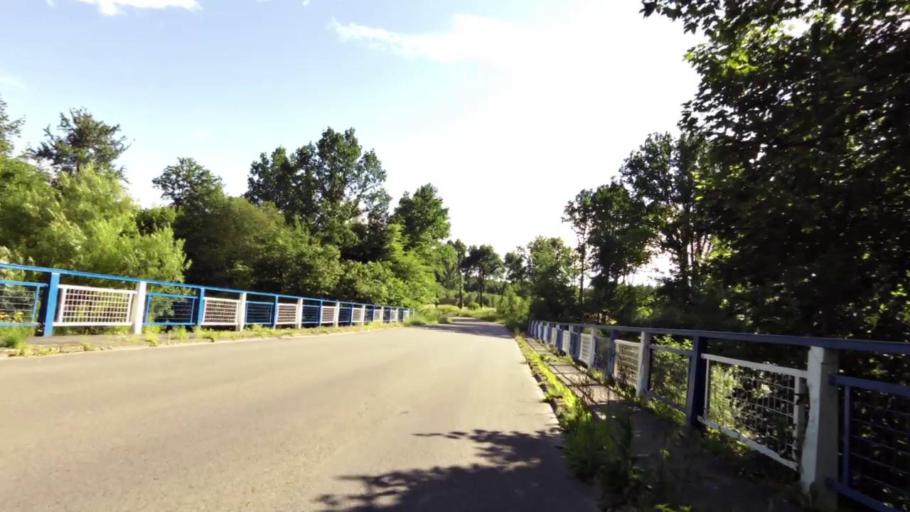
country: PL
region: West Pomeranian Voivodeship
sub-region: Powiat slawienski
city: Slawno
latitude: 54.4535
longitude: 16.7396
